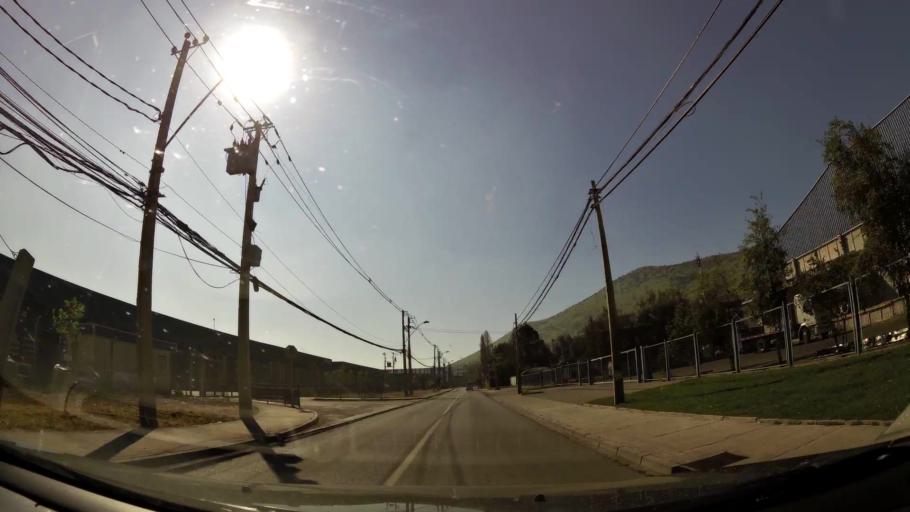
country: CL
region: Santiago Metropolitan
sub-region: Provincia de Chacabuco
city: Chicureo Abajo
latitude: -33.3367
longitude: -70.6961
